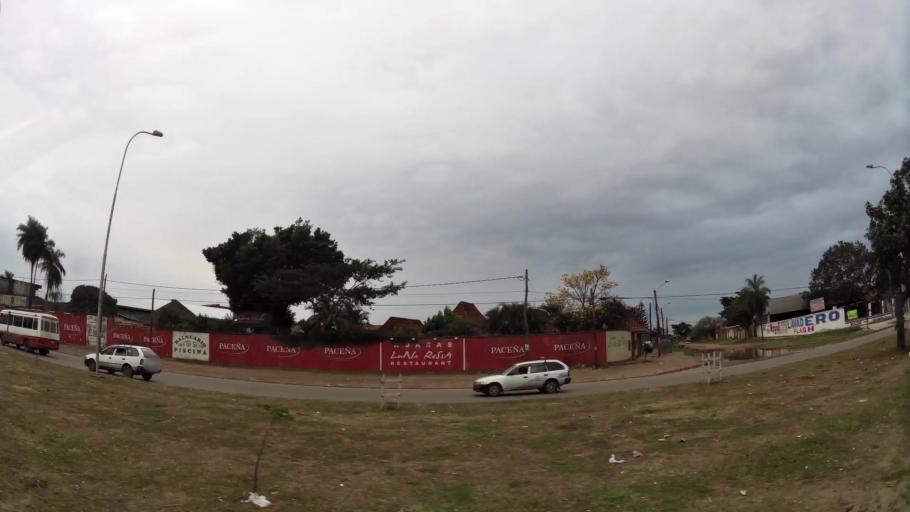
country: BO
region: Santa Cruz
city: Santa Cruz de la Sierra
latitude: -17.8366
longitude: -63.1832
